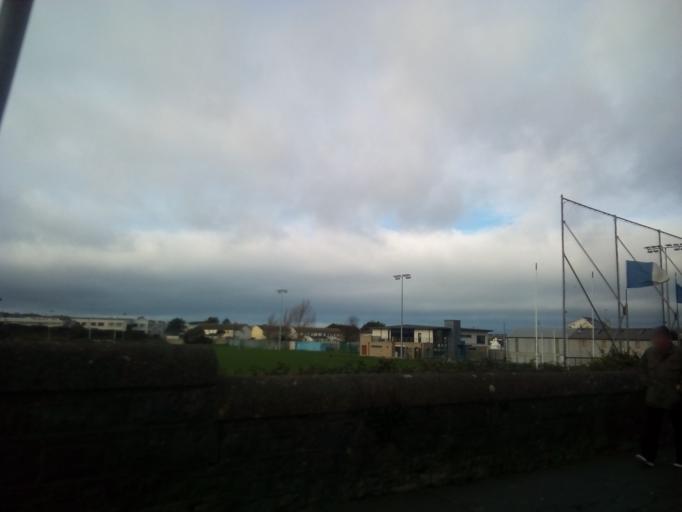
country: IE
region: Leinster
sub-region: Fingal County
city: Skerries
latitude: 53.5773
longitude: -6.1125
